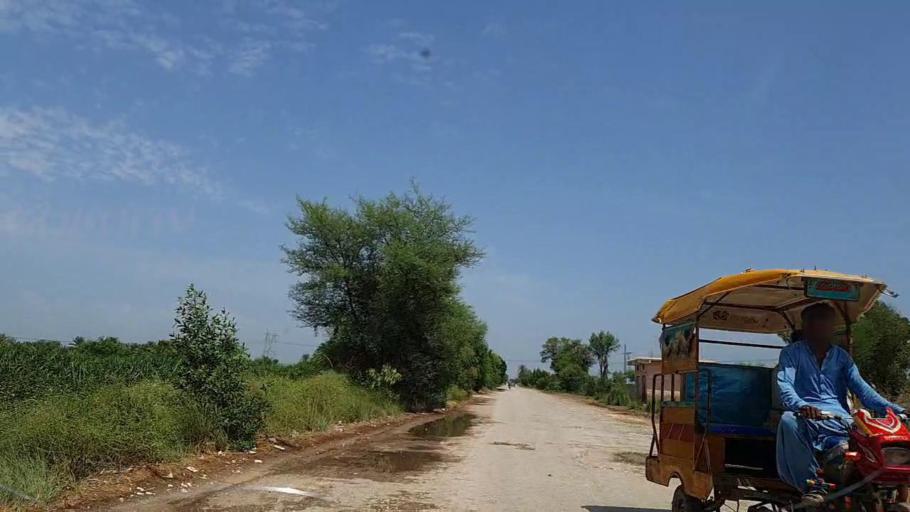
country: PK
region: Sindh
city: Naushahro Firoz
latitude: 26.8326
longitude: 68.1341
